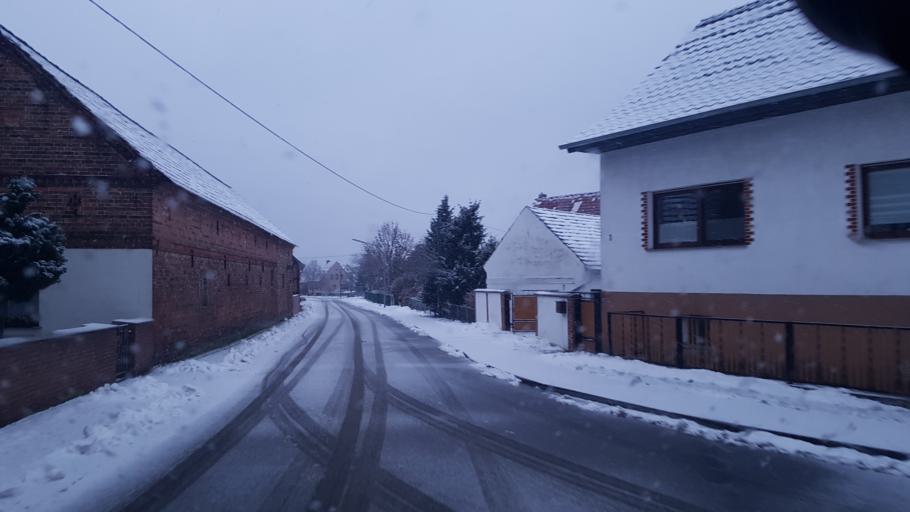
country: DE
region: Brandenburg
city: Janschwalde
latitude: 51.8988
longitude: 14.5148
